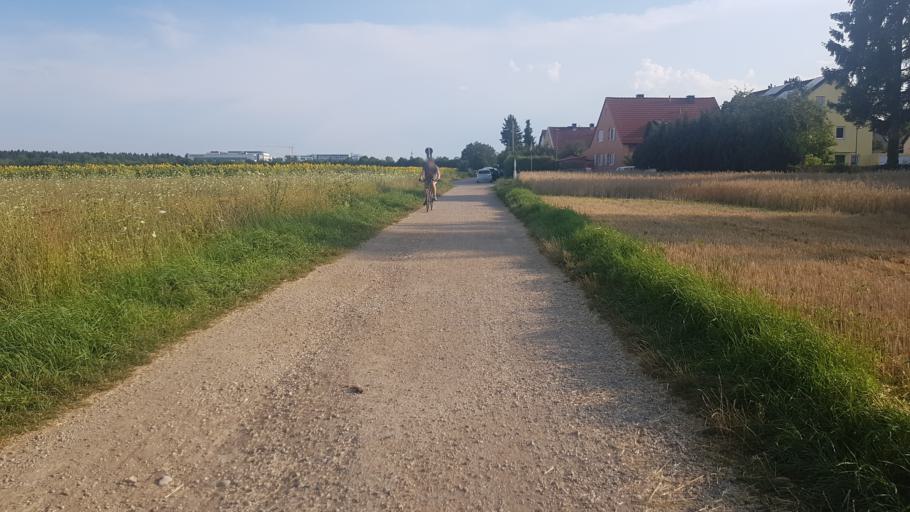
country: DE
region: Bavaria
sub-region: Upper Bavaria
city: Pasing
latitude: 48.1302
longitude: 11.4533
